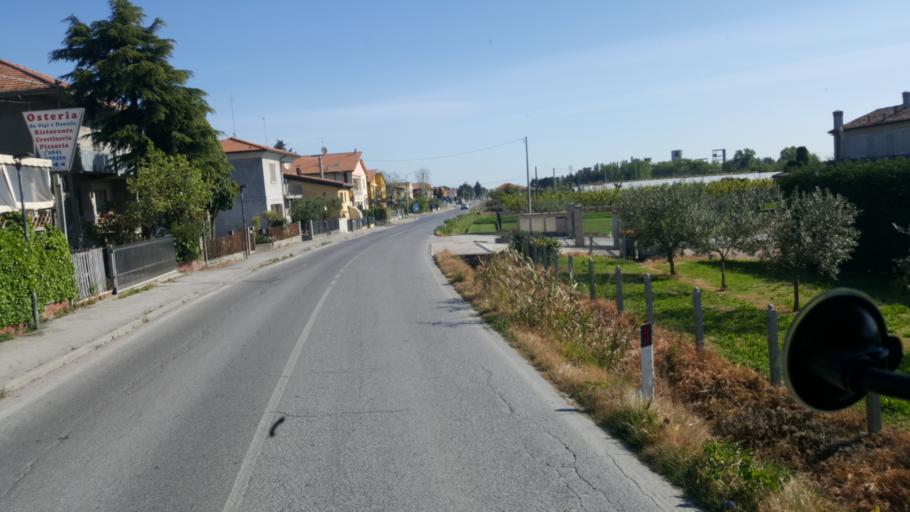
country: IT
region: Emilia-Romagna
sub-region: Provincia di Rimini
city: Sant'Andrea
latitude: 44.0318
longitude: 12.4189
